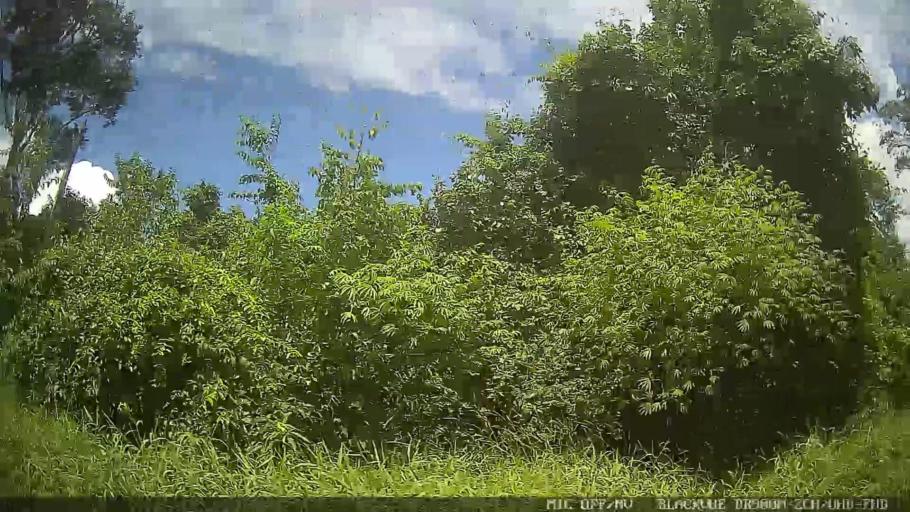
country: BR
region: Minas Gerais
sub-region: Extrema
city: Extrema
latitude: -22.7313
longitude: -46.4241
